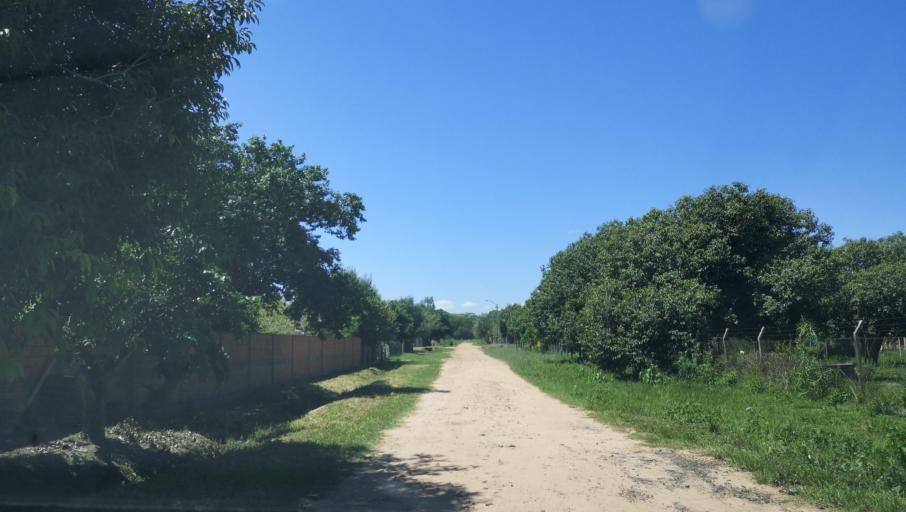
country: PY
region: Caaguazu
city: Carayao
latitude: -25.2018
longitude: -56.3987
